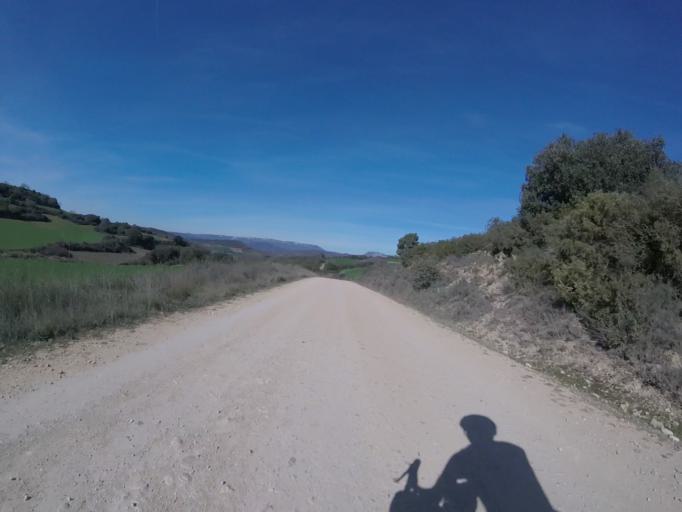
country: ES
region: Navarre
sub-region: Provincia de Navarra
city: Oteiza
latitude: 42.6436
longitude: -1.9590
